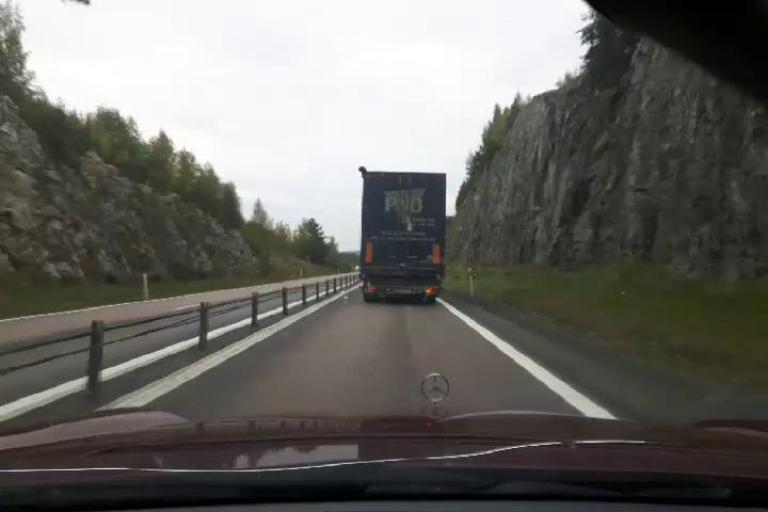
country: SE
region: Vaesternorrland
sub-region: Haernoesands Kommun
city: Haernoesand
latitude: 62.8269
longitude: 17.9687
